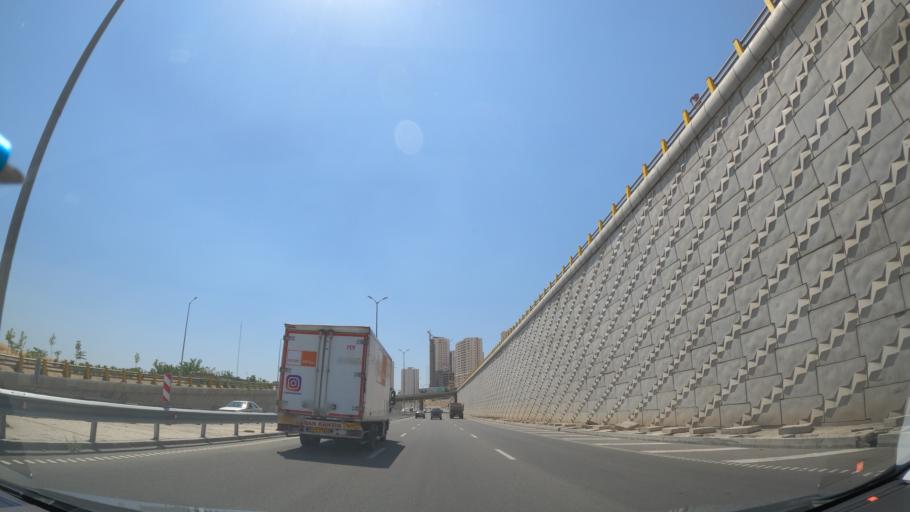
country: IR
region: Tehran
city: Shahr-e Qods
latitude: 35.7524
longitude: 51.1463
